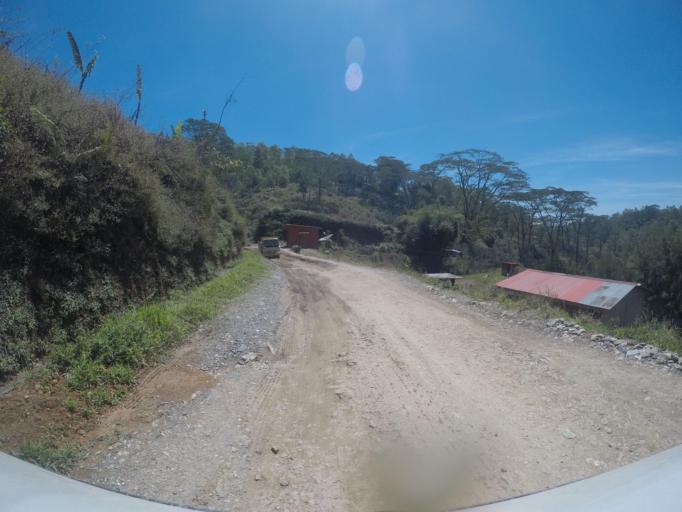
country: TL
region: Ermera
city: Gleno
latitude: -8.7735
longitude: 125.3984
